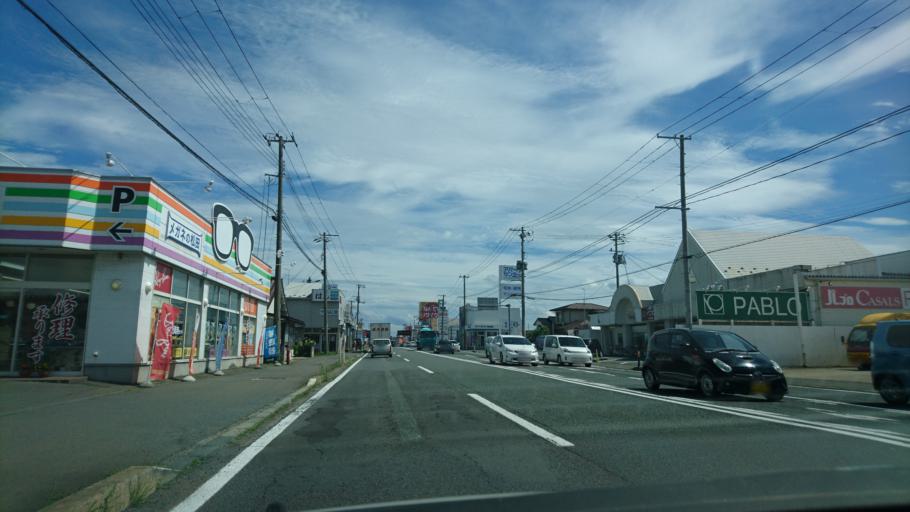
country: JP
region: Iwate
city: Morioka-shi
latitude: 39.6579
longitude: 141.1623
